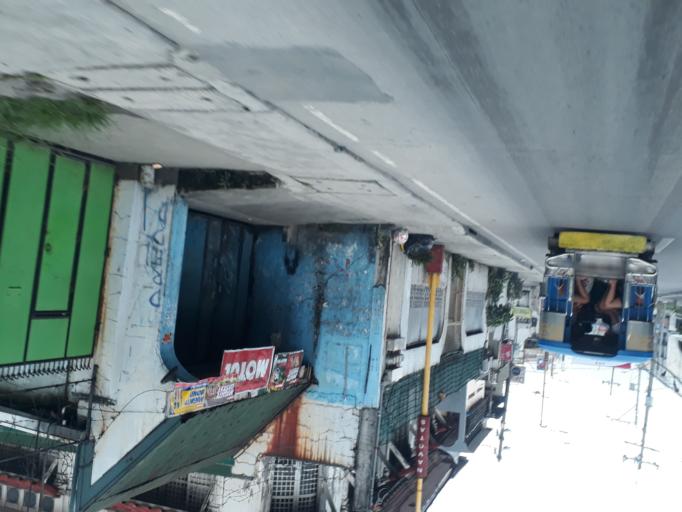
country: PH
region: Calabarzon
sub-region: Province of Rizal
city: Navotas
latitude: 14.6601
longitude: 120.9466
